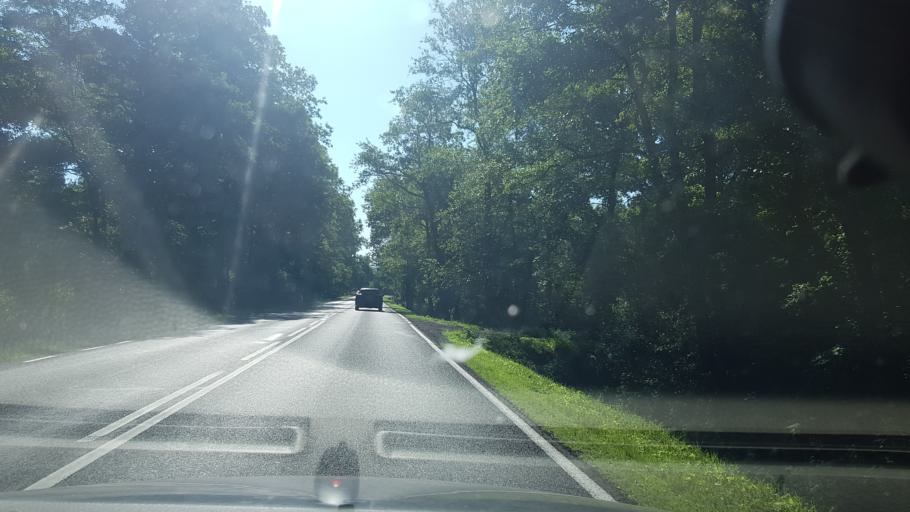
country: PL
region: Masovian Voivodeship
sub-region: Powiat wyszkowski
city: Wyszkow
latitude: 52.5866
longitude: 21.5178
